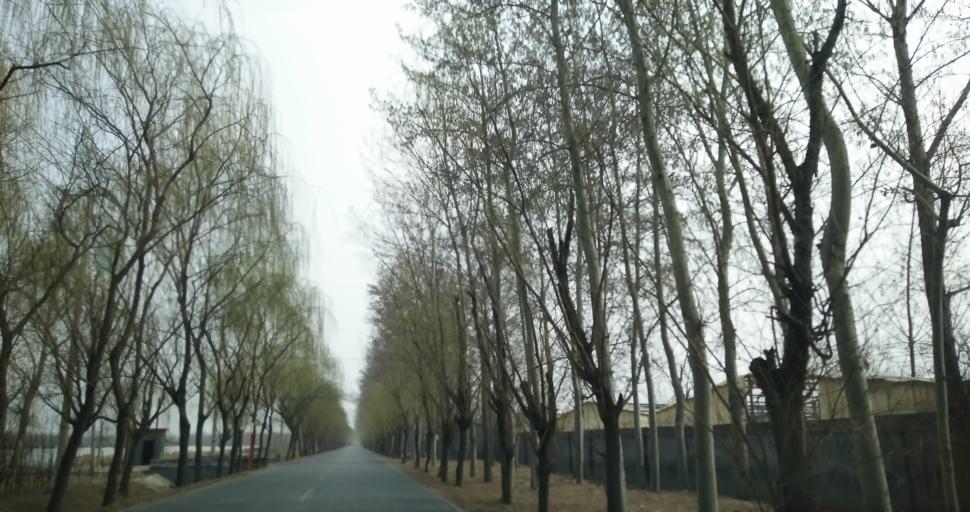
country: CN
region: Beijing
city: Qingyundian
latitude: 39.6982
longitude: 116.4936
